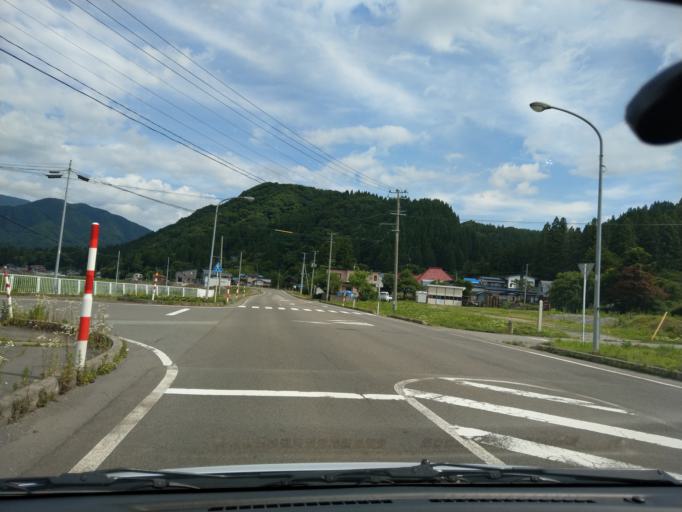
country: JP
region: Akita
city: Kakunodatemachi
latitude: 39.6753
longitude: 140.5656
